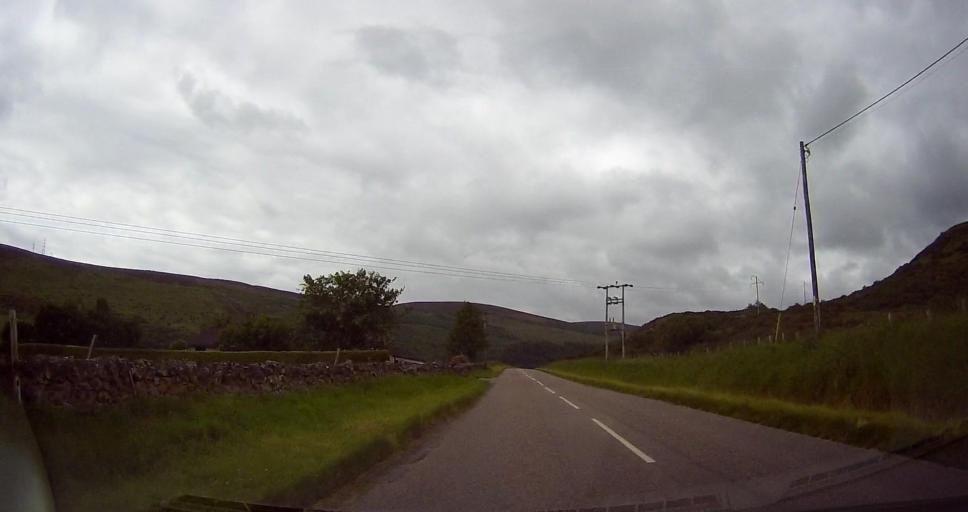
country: GB
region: Scotland
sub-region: Highland
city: Dornoch
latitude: 57.9840
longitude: -4.1347
